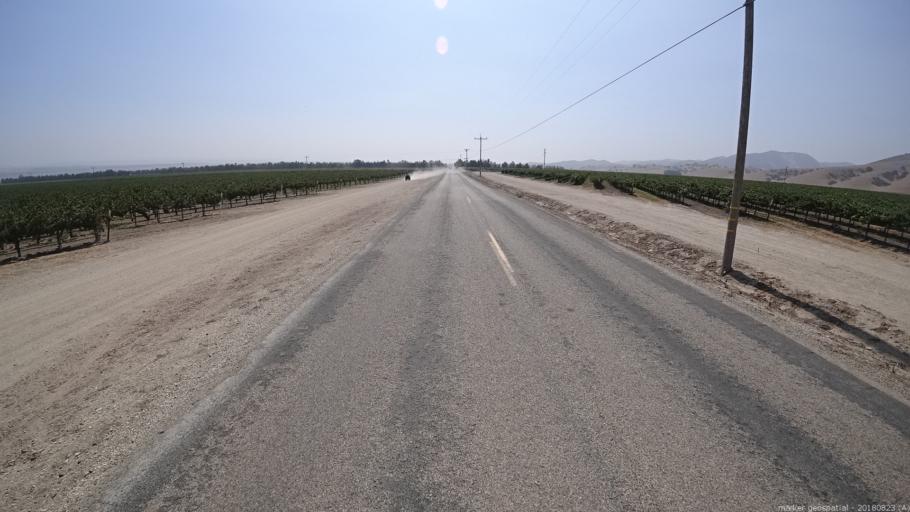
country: US
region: California
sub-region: Monterey County
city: Greenfield
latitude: 36.2528
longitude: -121.1990
